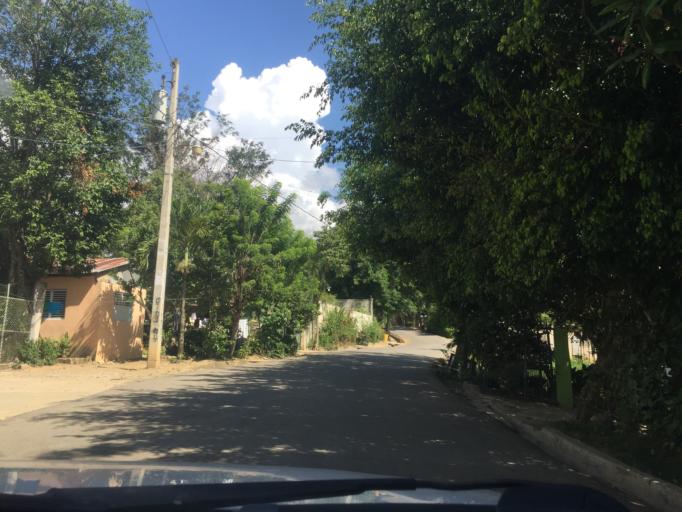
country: DO
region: La Vega
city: Rio Verde Arriba
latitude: 19.3570
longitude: -70.5910
